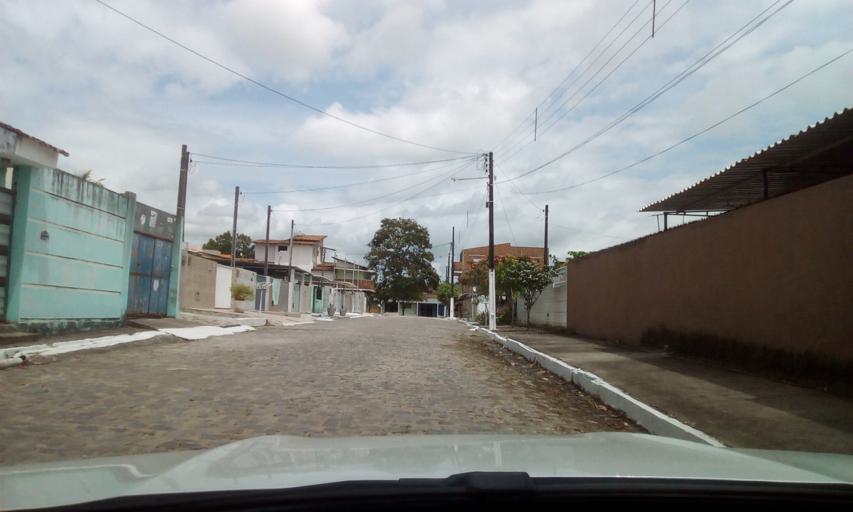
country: BR
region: Paraiba
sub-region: Bayeux
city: Bayeux
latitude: -7.1349
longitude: -34.9523
